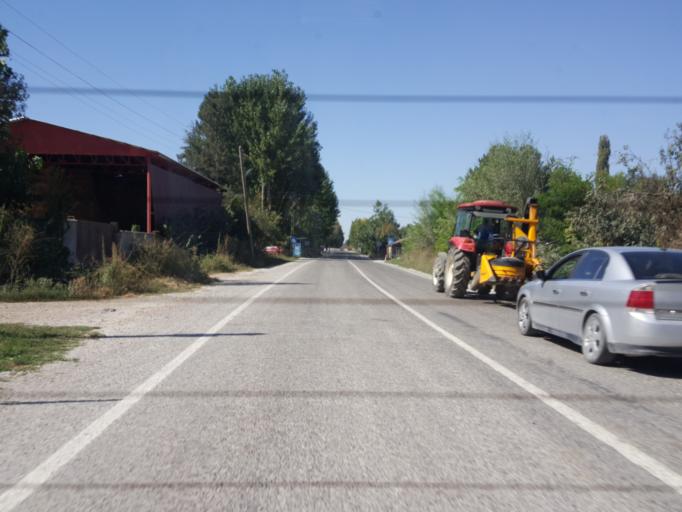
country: TR
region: Tokat
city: Pazar
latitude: 40.2703
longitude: 36.2454
